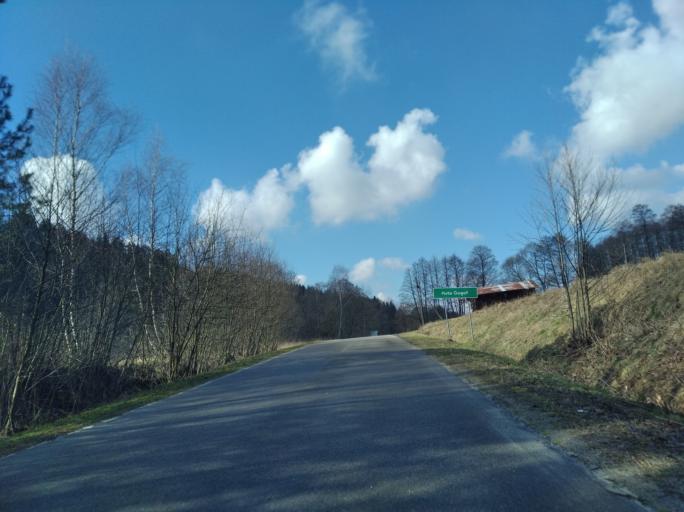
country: PL
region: Subcarpathian Voivodeship
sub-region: Powiat strzyzowski
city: Frysztak
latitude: 49.8669
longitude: 21.5410
